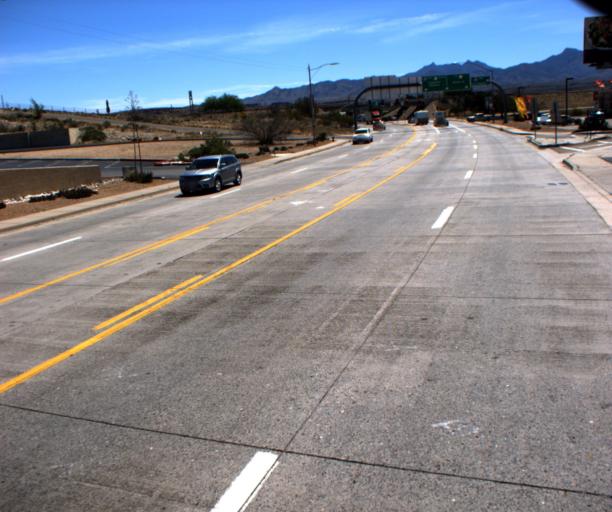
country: US
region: Arizona
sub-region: Mohave County
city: Kingman
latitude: 35.1916
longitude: -114.0698
